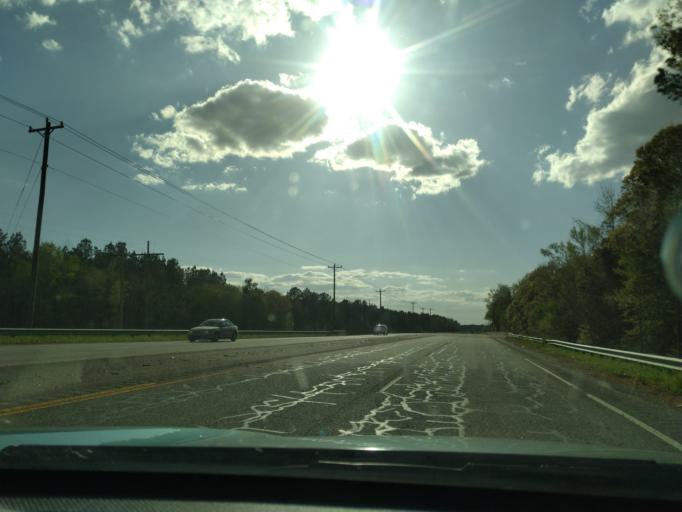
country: US
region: South Carolina
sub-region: Williamsburg County
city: Kingstree
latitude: 33.6578
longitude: -79.8563
